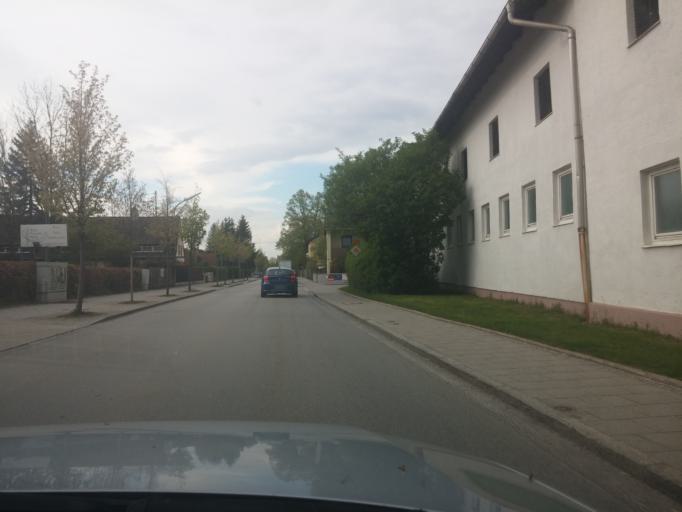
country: DE
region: Bavaria
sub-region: Upper Bavaria
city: Feldkirchen
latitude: 48.1286
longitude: 11.7403
